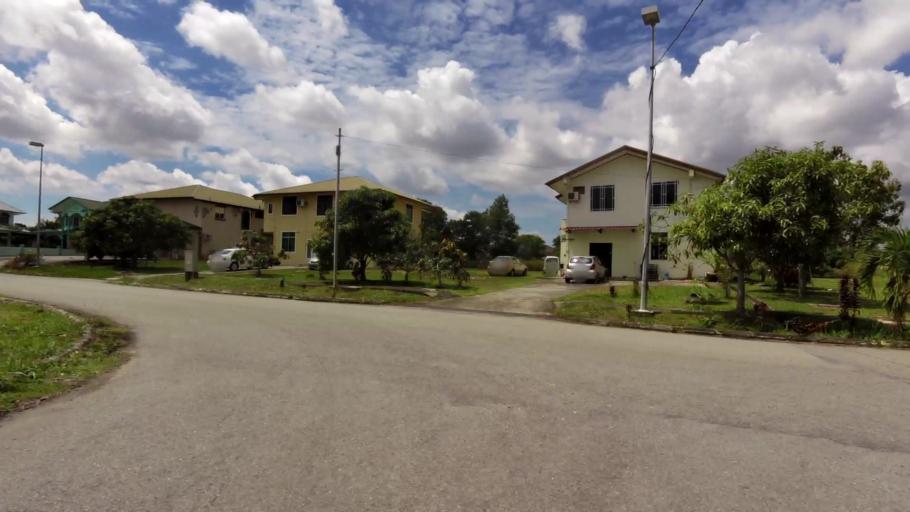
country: BN
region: Brunei and Muara
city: Bandar Seri Begawan
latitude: 4.9488
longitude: 114.9111
